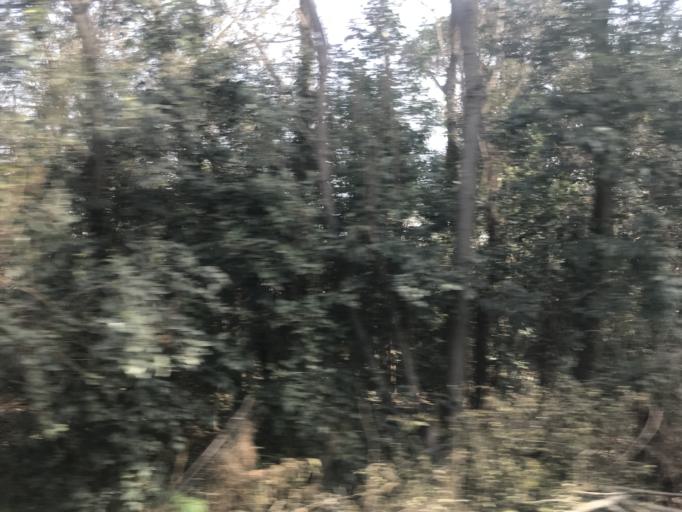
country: AR
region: Cordoba
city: Laguna Larga
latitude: -31.8067
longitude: -63.7771
